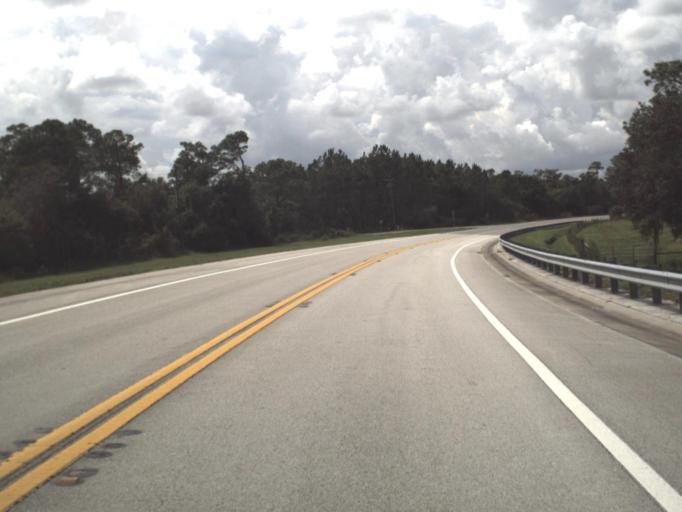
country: US
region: Florida
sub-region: DeSoto County
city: Nocatee
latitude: 27.1997
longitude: -81.9890
